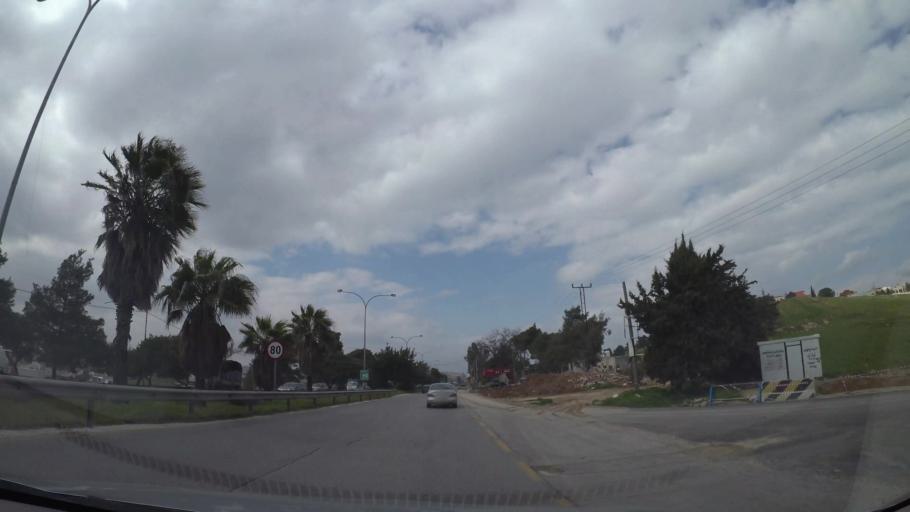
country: JO
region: Balqa
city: As Salt
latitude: 32.0355
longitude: 35.7913
